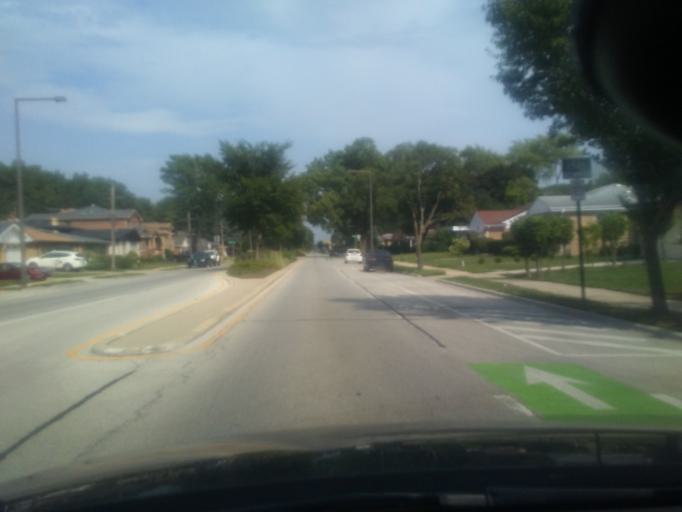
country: US
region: Illinois
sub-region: Cook County
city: Skokie
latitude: 42.0335
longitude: -87.7412
